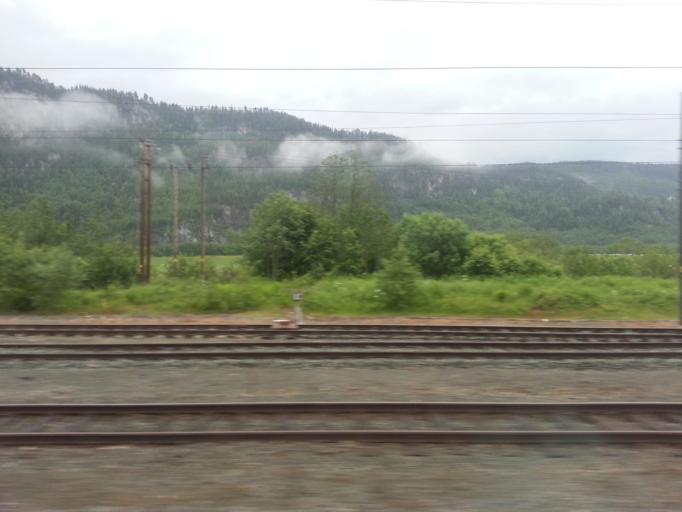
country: NO
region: Sor-Trondelag
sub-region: Midtre Gauldal
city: Storen
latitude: 63.0507
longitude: 10.2850
